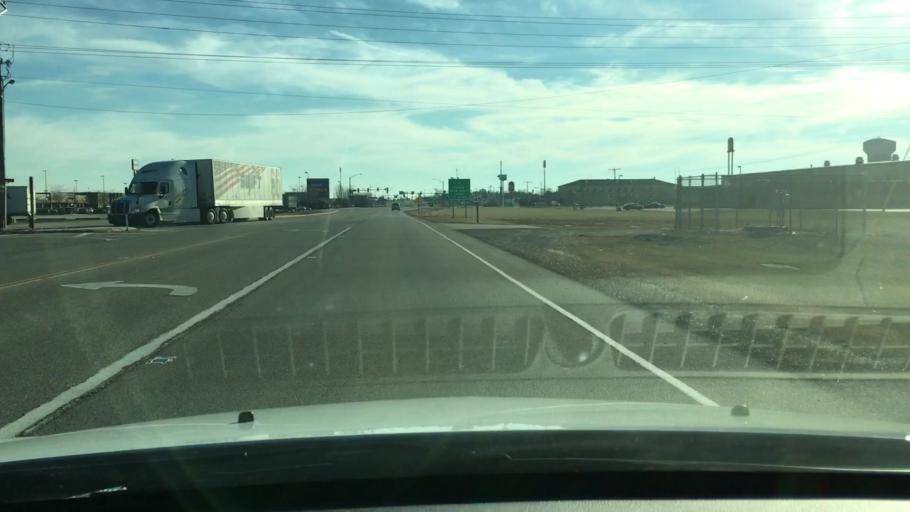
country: US
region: Illinois
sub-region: LaSalle County
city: Peru
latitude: 41.3750
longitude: -89.1256
